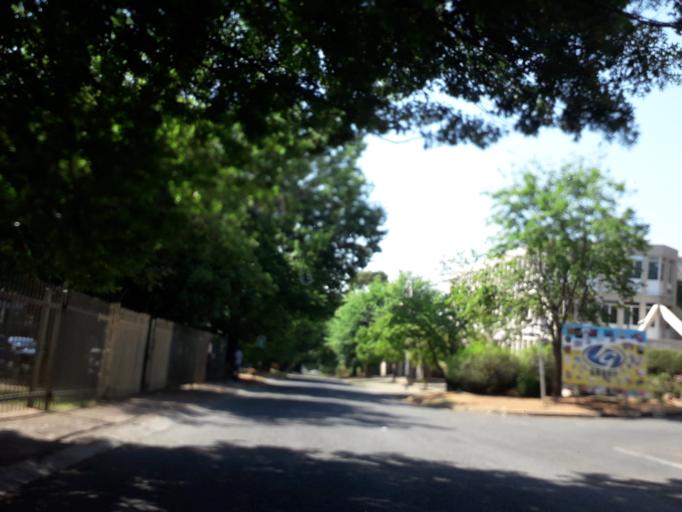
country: ZA
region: Gauteng
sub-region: City of Johannesburg Metropolitan Municipality
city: Johannesburg
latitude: -26.0975
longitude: 28.0080
